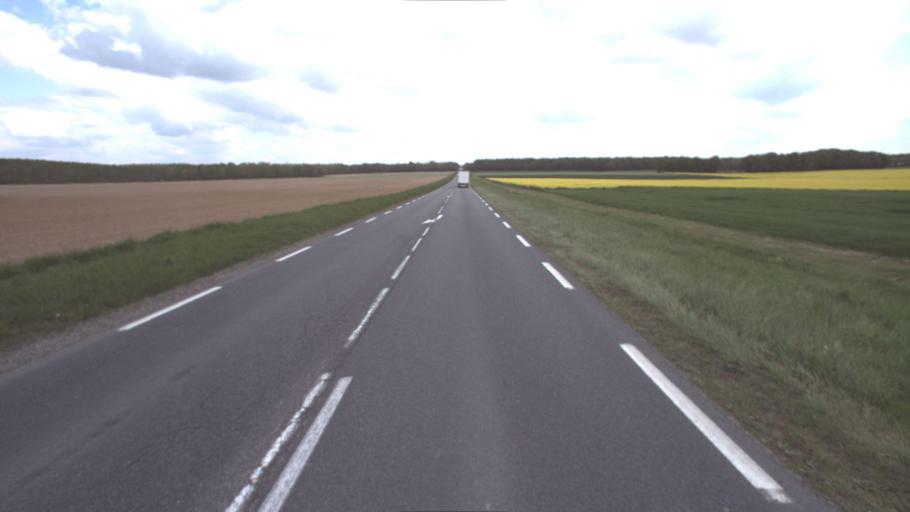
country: FR
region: Ile-de-France
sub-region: Departement de Seine-et-Marne
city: Villiers-Saint-Georges
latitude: 48.6986
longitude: 3.4486
